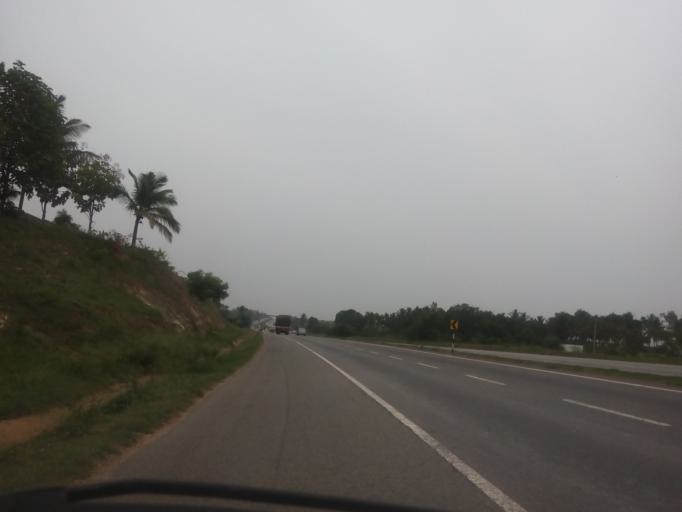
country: IN
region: Karnataka
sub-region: Bangalore Urban
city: Bangalore
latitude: 12.9829
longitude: 77.4708
